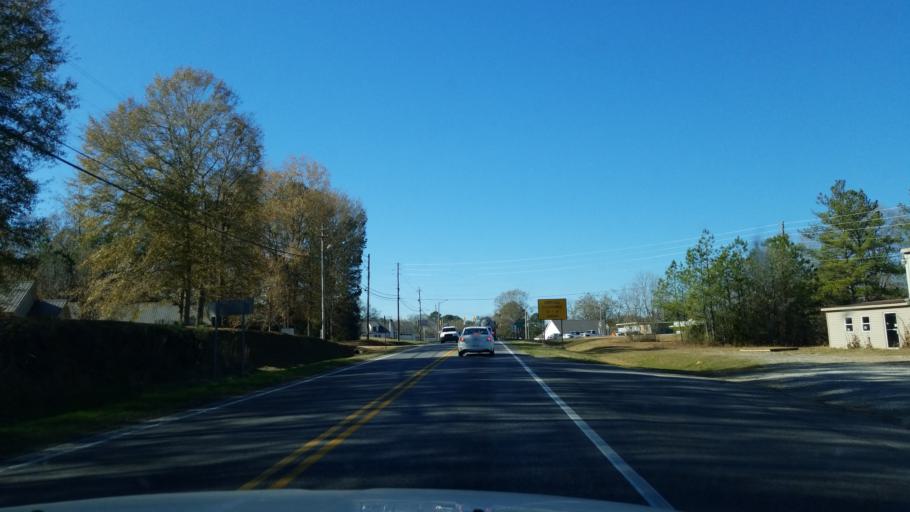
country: US
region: Alabama
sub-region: Pickens County
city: Gordo
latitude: 33.3157
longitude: -87.9011
